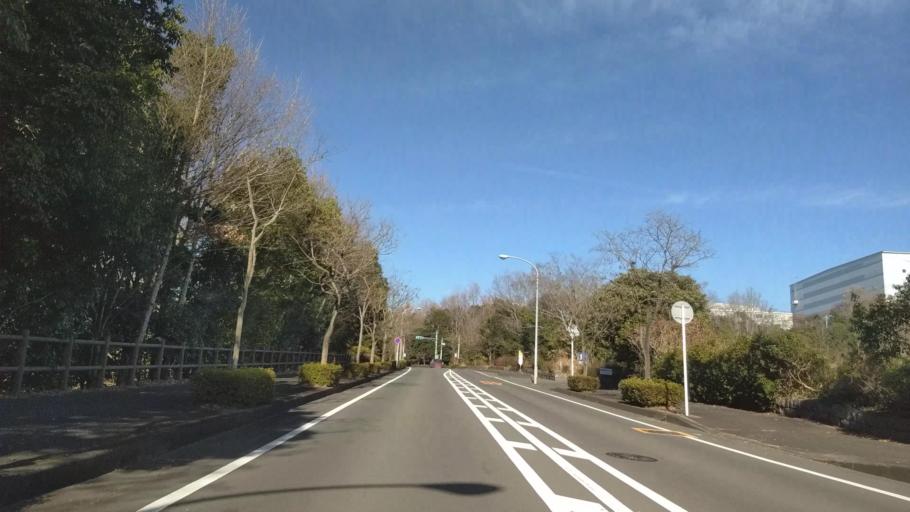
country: JP
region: Kanagawa
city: Hadano
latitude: 35.3434
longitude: 139.2219
